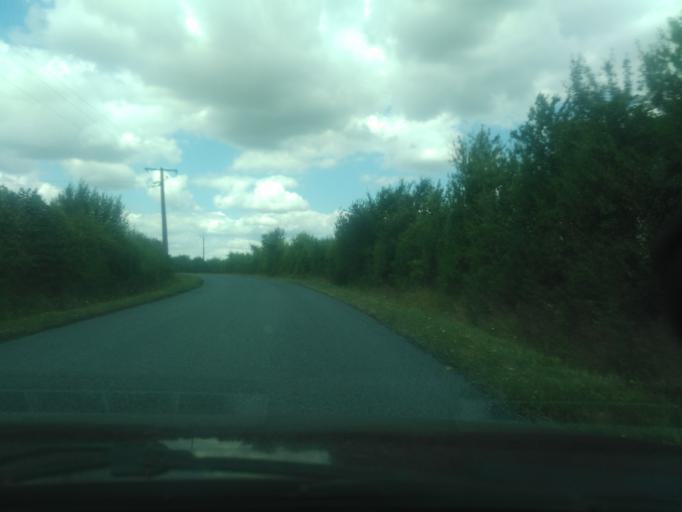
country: FR
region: Pays de la Loire
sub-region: Departement de la Vendee
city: Les Brouzils
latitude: 46.8740
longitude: -1.3209
